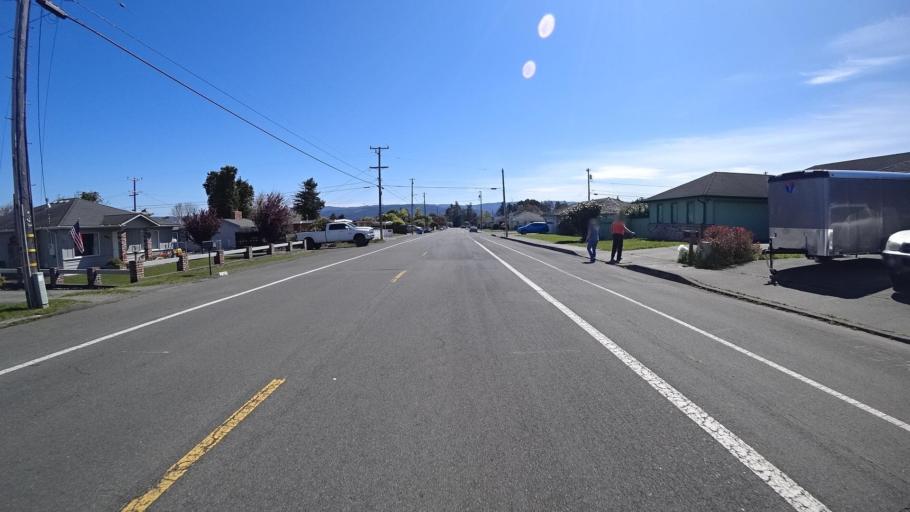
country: US
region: California
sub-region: Humboldt County
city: Myrtletown
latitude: 40.7878
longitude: -124.1292
